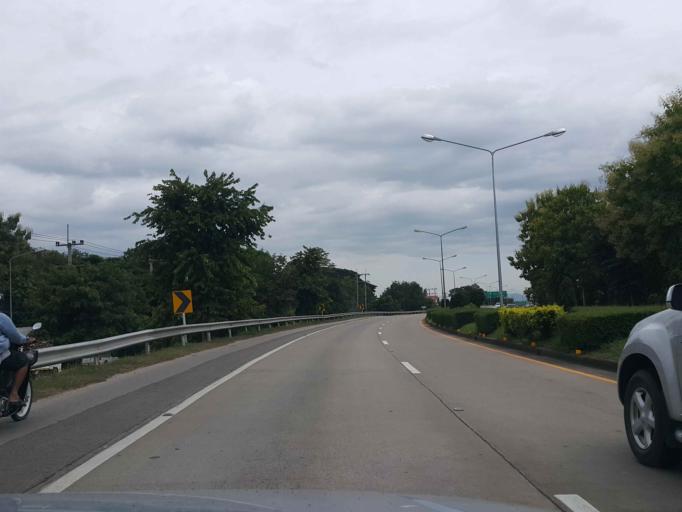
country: TH
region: Lampang
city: Lampang
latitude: 18.2719
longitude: 99.4620
